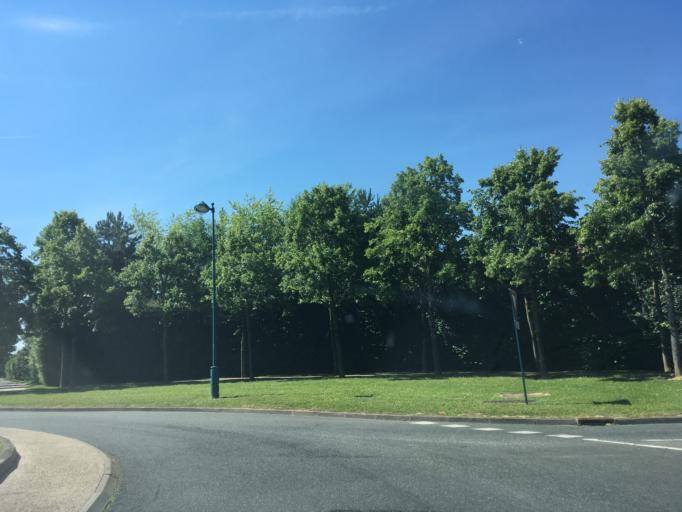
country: FR
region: Ile-de-France
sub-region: Departement de Seine-et-Marne
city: Magny-le-Hongre
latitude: 48.8592
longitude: 2.8137
